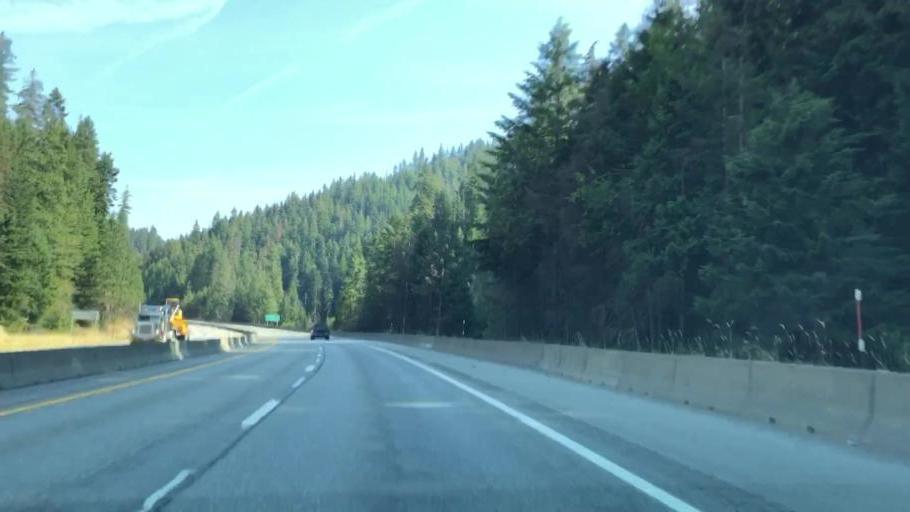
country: US
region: Idaho
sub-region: Kootenai County
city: Coeur d'Alene
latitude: 47.6289
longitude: -116.5971
